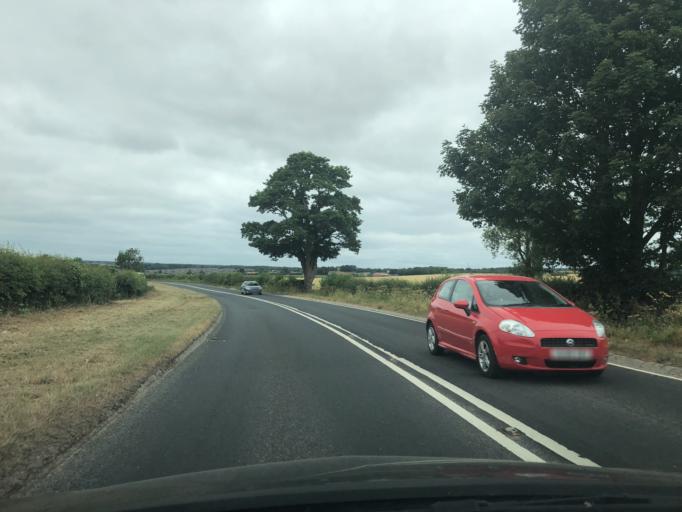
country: GB
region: England
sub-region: North Yorkshire
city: East Ayton
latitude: 54.2478
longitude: -0.4552
